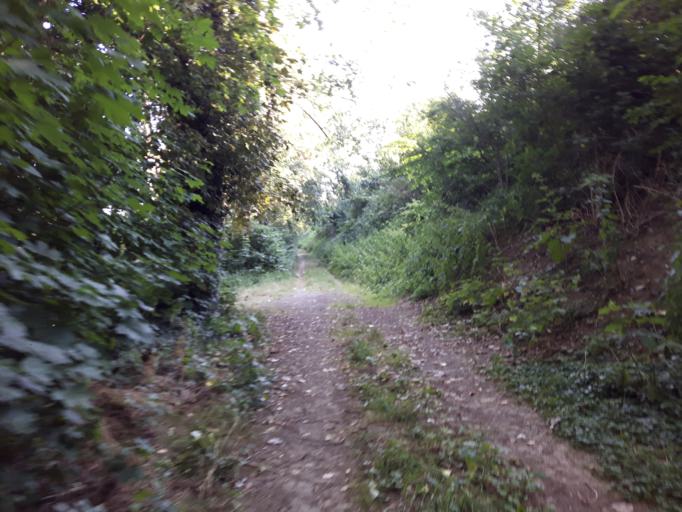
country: DE
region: Baden-Wuerttemberg
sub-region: Karlsruhe Region
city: Karlsdorf-Neuthard
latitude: 49.0985
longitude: 8.5371
